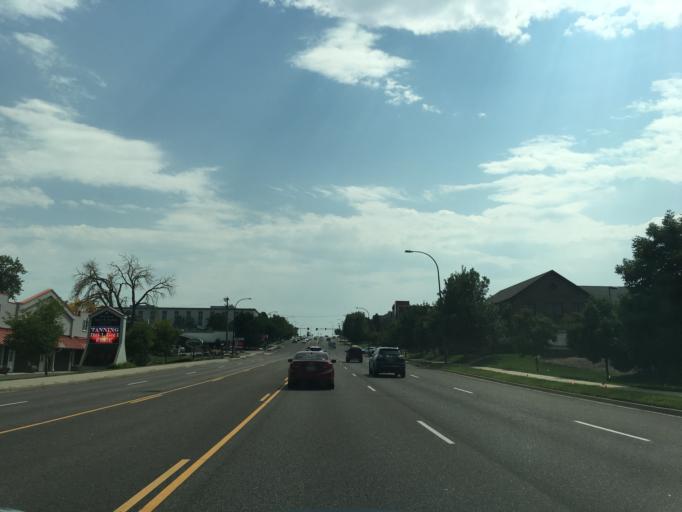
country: US
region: Colorado
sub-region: Jefferson County
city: Applewood
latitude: 39.7322
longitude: -105.1285
